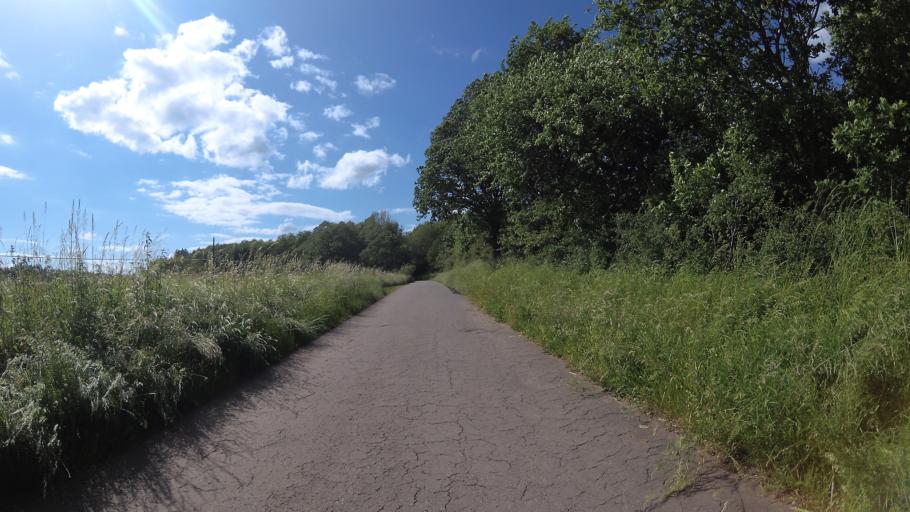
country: DE
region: Saarland
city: Ottweiler
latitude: 49.4157
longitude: 7.1443
